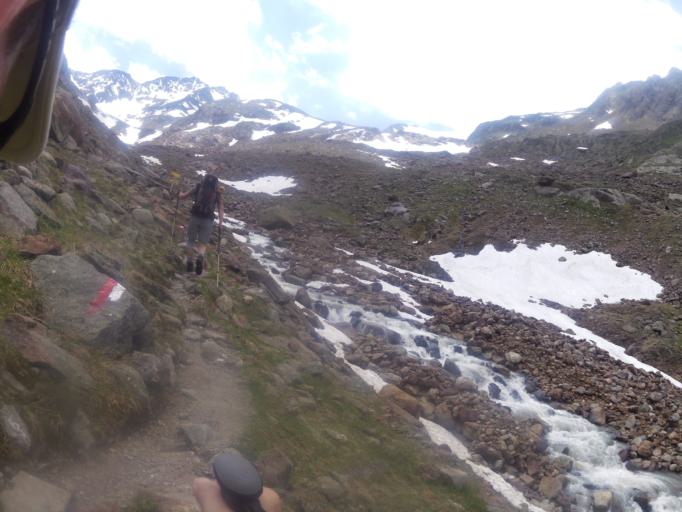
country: IT
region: Trentino-Alto Adige
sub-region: Bolzano
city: Racines
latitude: 46.9881
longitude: 11.2252
